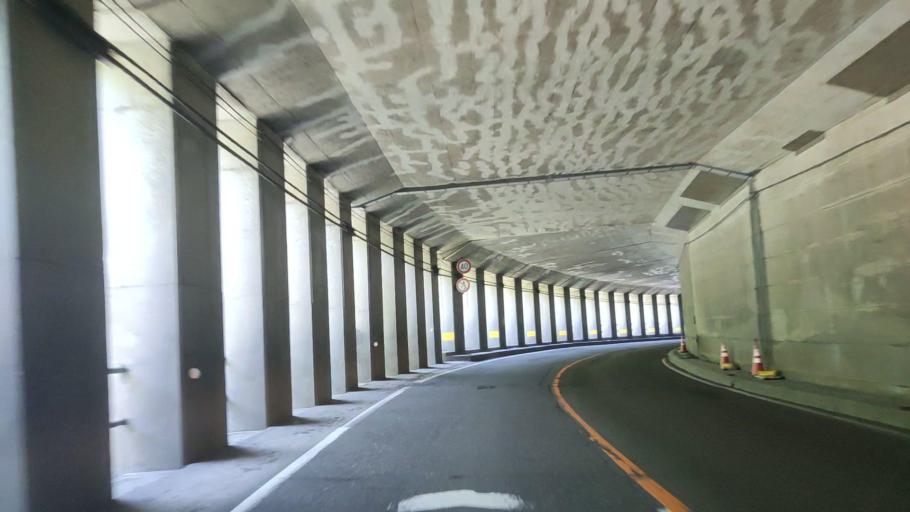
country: JP
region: Niigata
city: Itoigawa
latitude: 36.9049
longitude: 137.8667
